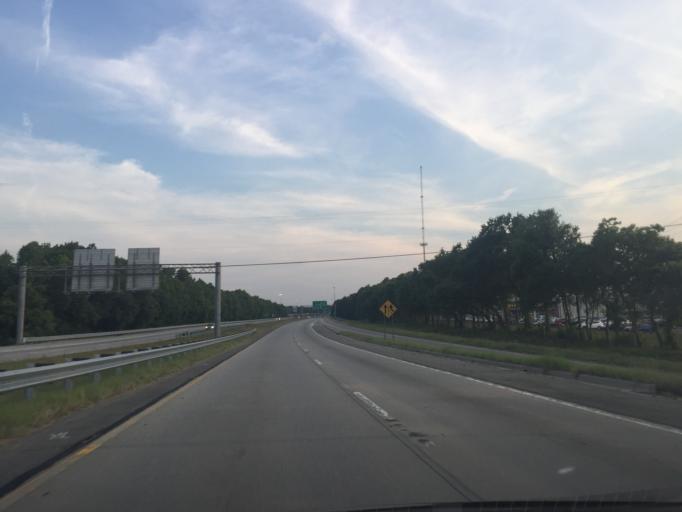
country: US
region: Georgia
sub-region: Chatham County
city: Savannah
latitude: 32.0526
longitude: -81.1422
